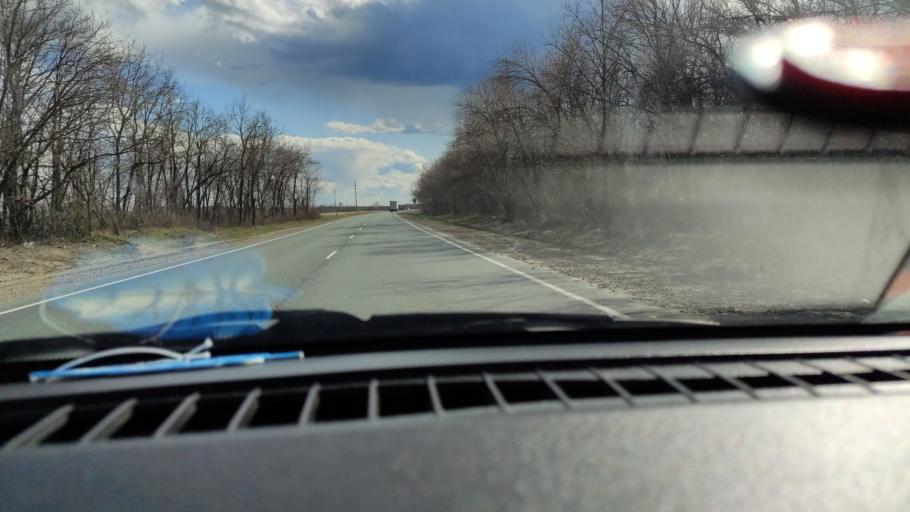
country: RU
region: Saratov
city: Alekseyevka
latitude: 52.2684
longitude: 47.9272
